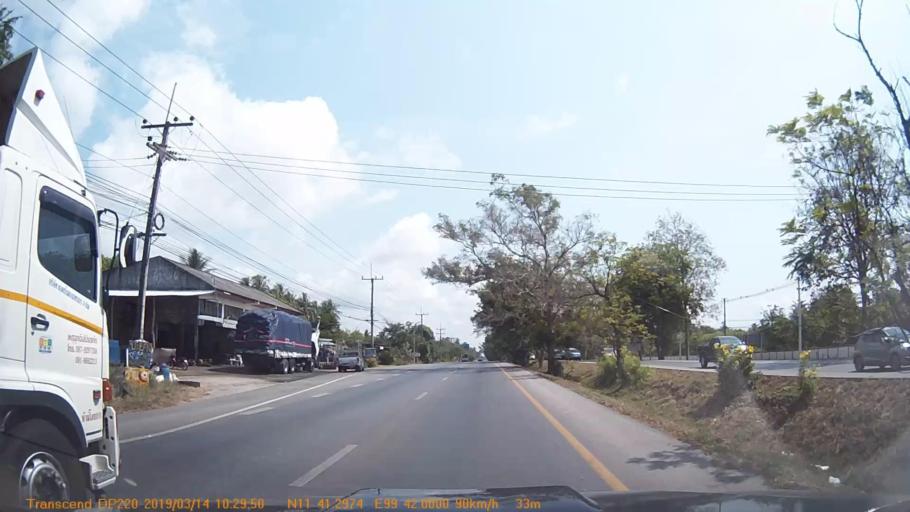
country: TH
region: Prachuap Khiri Khan
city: Prachuap Khiri Khan
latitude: 11.6801
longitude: 99.6939
